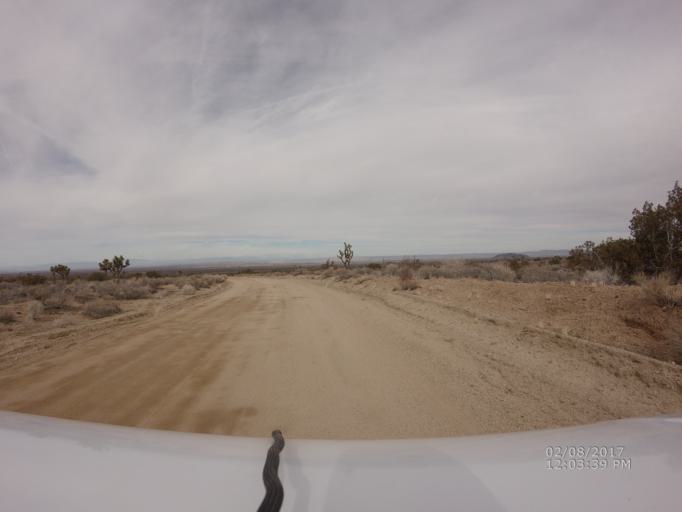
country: US
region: California
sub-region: San Bernardino County
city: Pinon Hills
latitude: 34.4701
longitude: -117.7753
